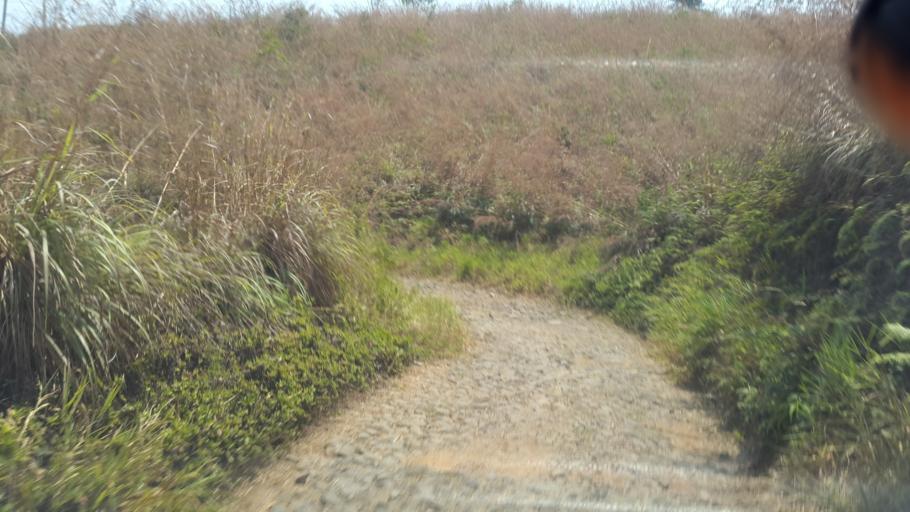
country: ID
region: West Java
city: Cihaur Girang
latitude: -7.1011
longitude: 106.5659
